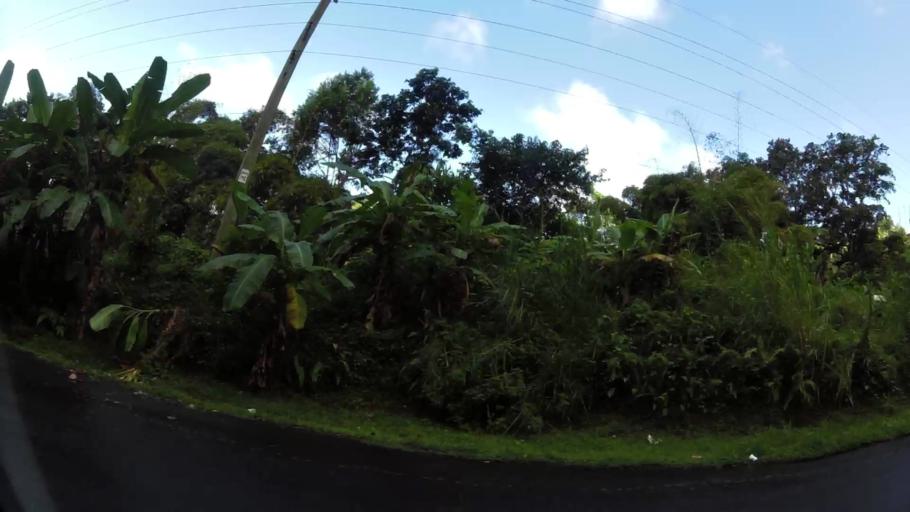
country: LC
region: Soufriere
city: Soufriere
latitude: 13.8728
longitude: -61.0423
